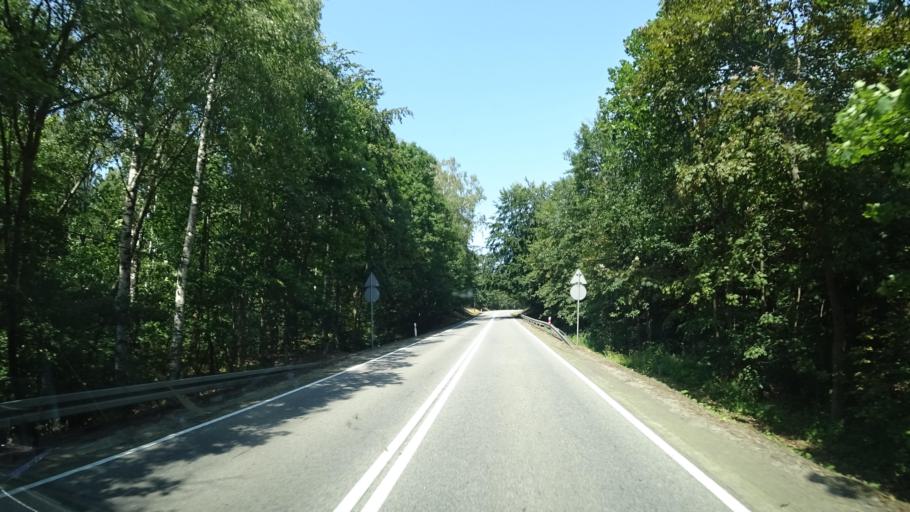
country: PL
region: Pomeranian Voivodeship
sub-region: Powiat koscierski
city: Grabowo Koscierskie
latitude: 54.2076
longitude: 18.1143
